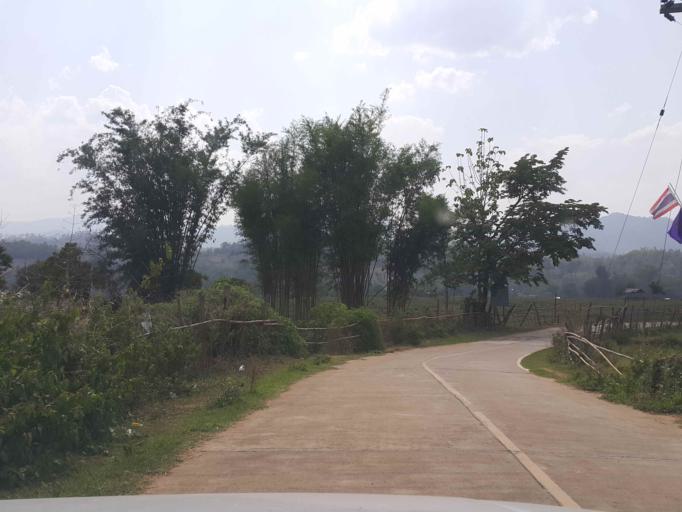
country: TH
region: Chiang Mai
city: Wiang Haeng
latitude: 19.3790
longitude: 98.7202
